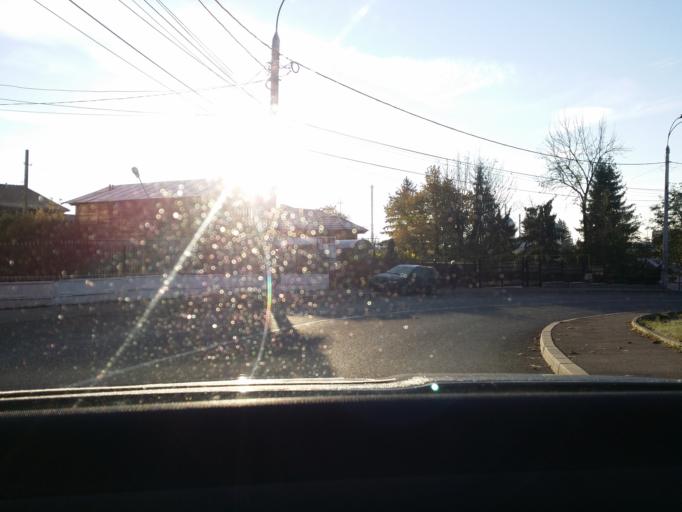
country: RO
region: Prahova
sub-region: Municipiul Campina
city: Campina
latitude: 45.1343
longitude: 25.7330
